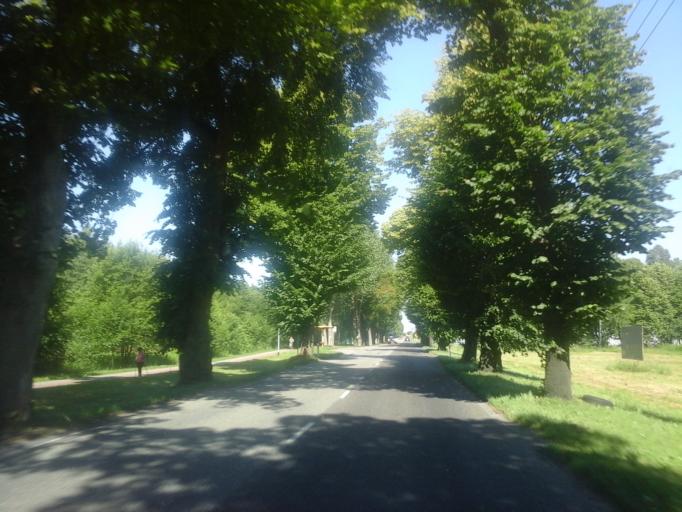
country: PL
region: West Pomeranian Voivodeship
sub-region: Powiat bialogardzki
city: Bialogard
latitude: 54.0169
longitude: 15.9503
